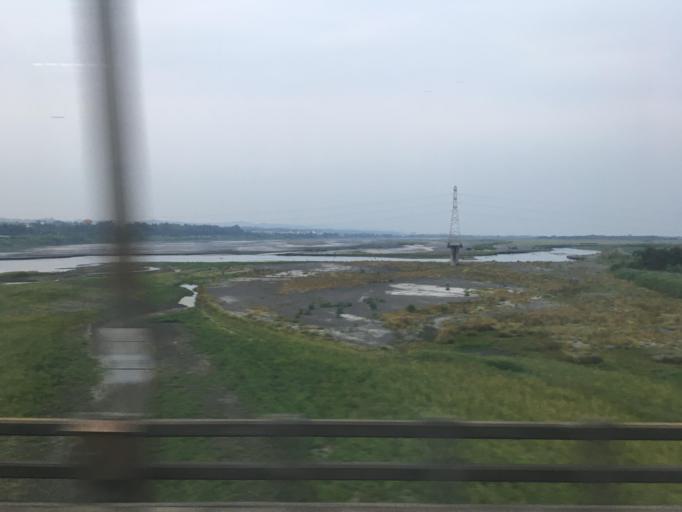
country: TW
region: Taiwan
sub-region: Pingtung
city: Pingtung
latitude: 22.6623
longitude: 120.4339
